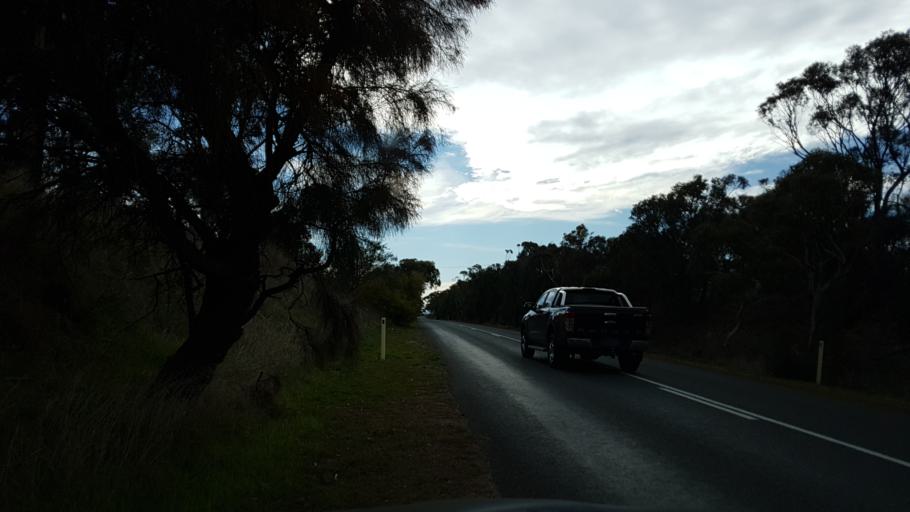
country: AU
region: South Australia
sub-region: Mount Barker
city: Macclesfield
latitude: -35.1572
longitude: 138.9348
